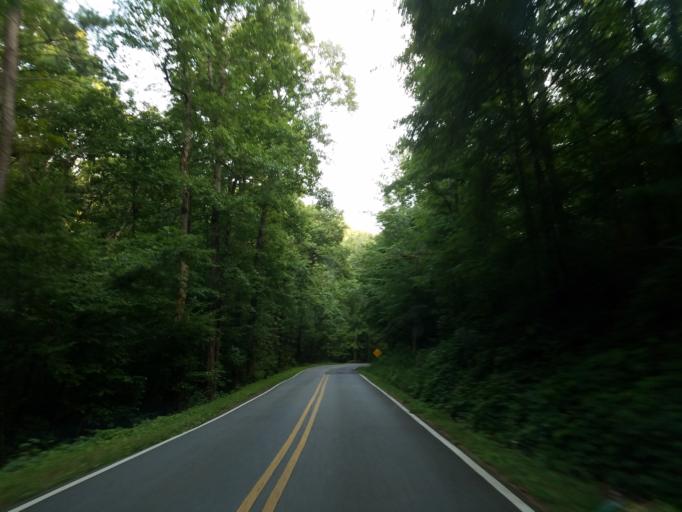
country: US
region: Georgia
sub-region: Pickens County
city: Jasper
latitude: 34.4850
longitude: -84.4175
